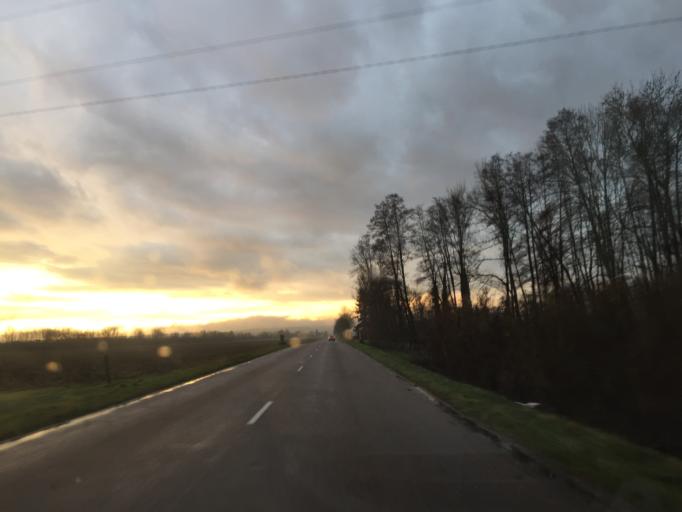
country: FR
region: Franche-Comte
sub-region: Departement du Jura
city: Choisey
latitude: 47.0399
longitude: 5.4955
